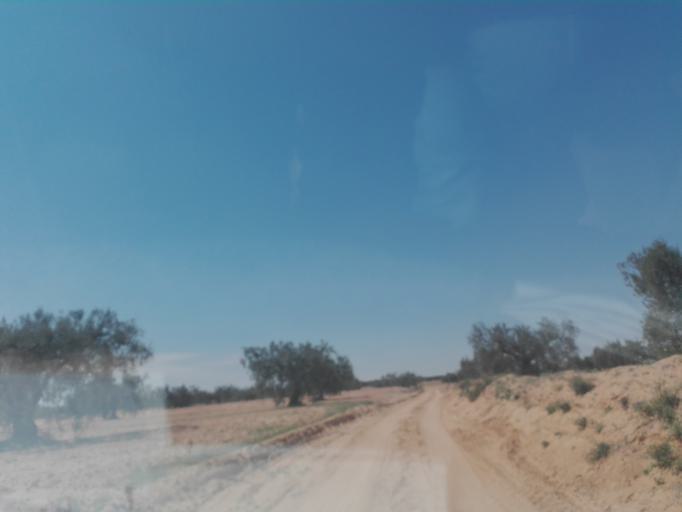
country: TN
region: Safaqis
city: Bi'r `Ali Bin Khalifah
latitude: 34.6073
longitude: 10.3522
